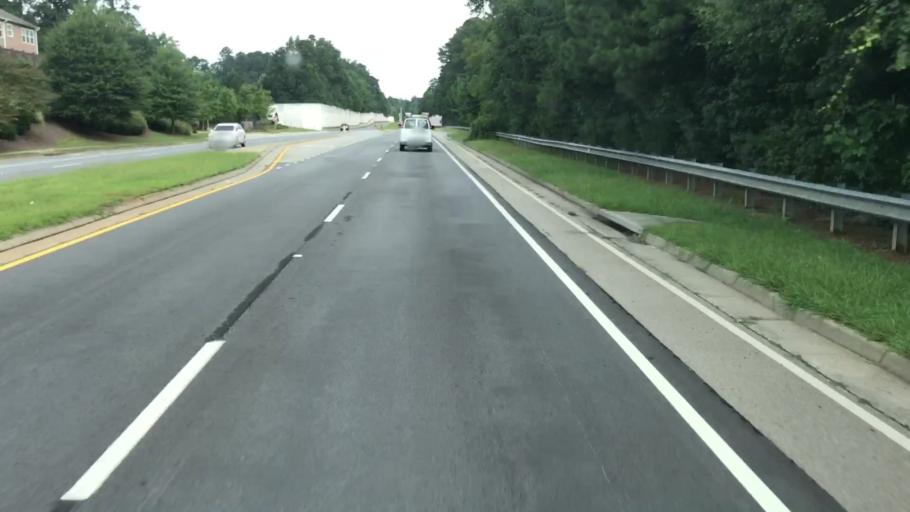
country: US
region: Georgia
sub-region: Gwinnett County
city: Duluth
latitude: 33.9694
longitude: -84.0702
